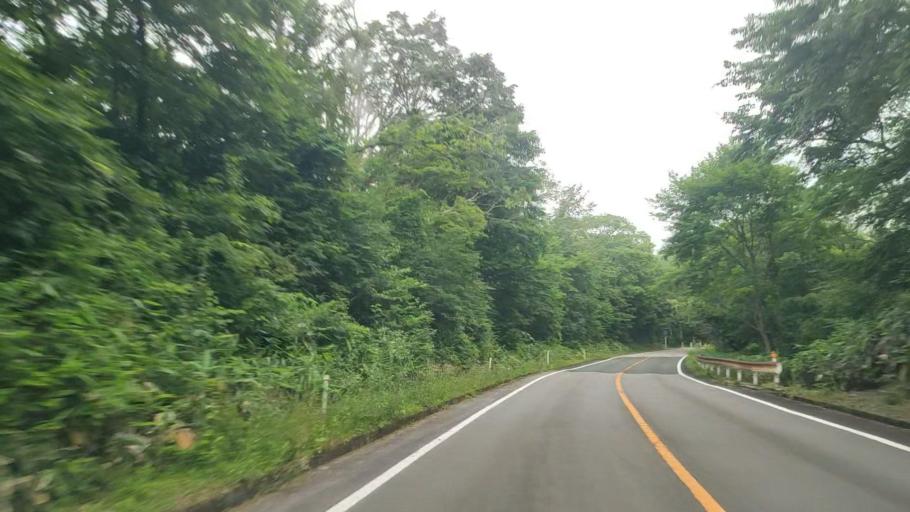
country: JP
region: Tottori
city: Kurayoshi
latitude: 35.3079
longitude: 133.6161
